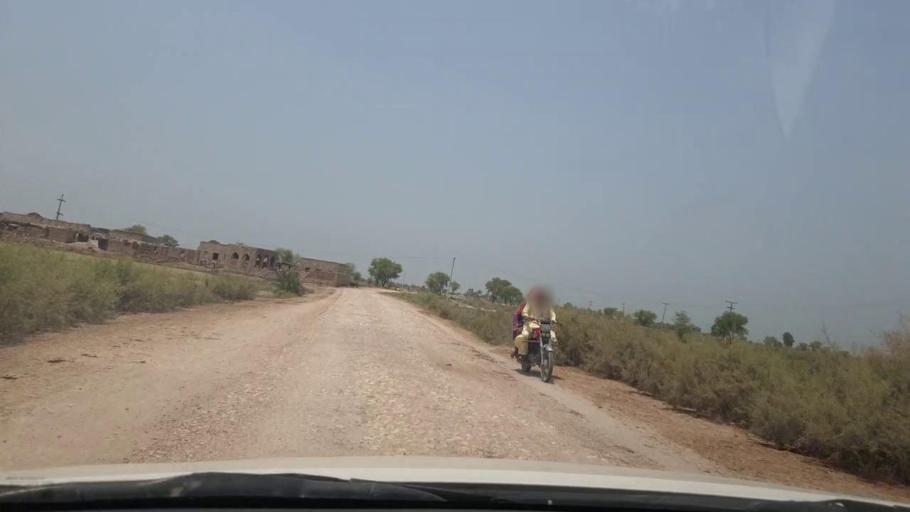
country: PK
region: Sindh
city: Rustam jo Goth
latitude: 28.0357
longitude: 68.7561
